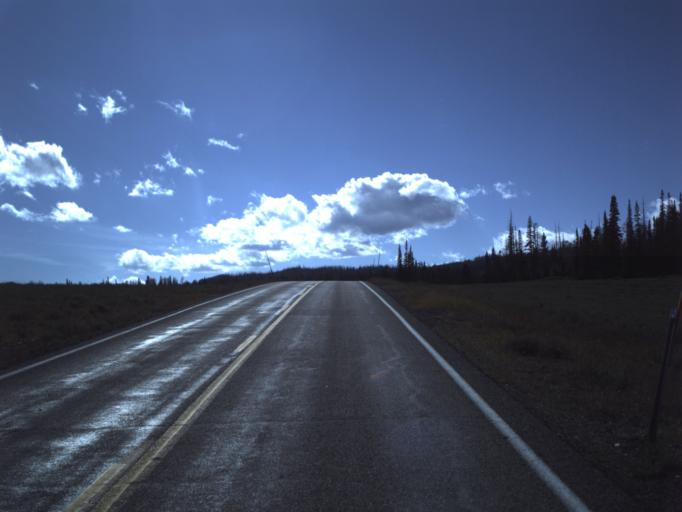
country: US
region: Utah
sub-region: Iron County
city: Parowan
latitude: 37.6510
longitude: -112.7861
